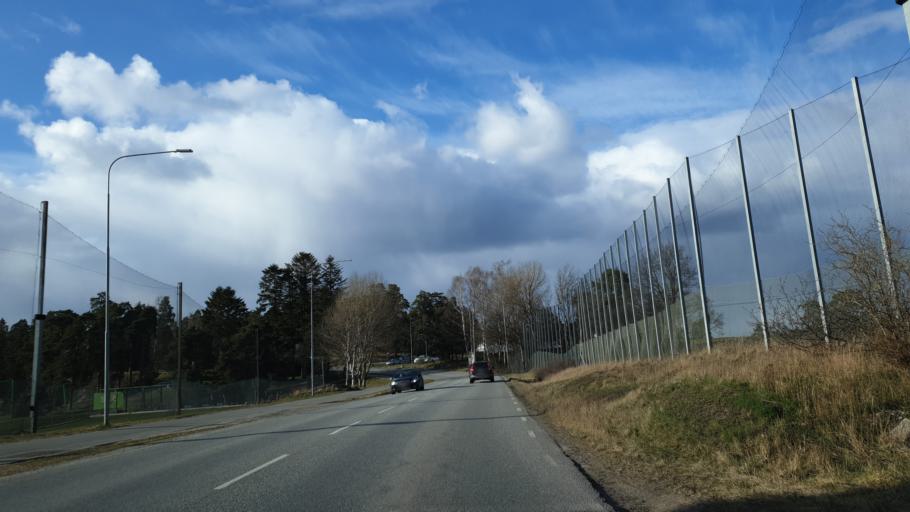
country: SE
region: Stockholm
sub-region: Lidingo
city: Lidingoe
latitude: 59.3777
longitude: 18.1274
